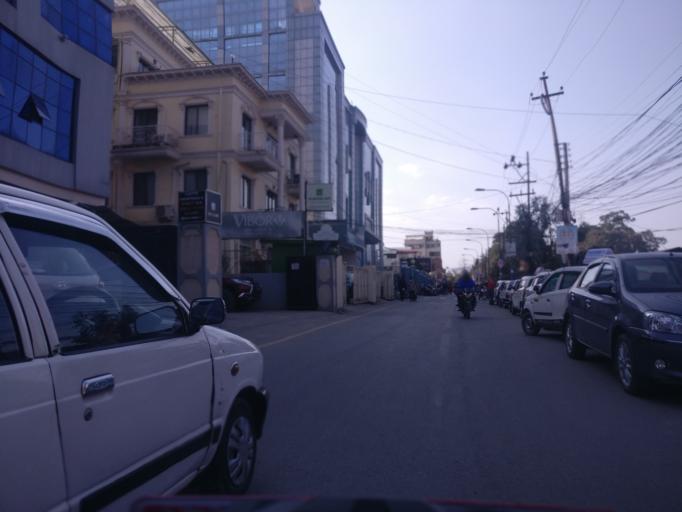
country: NP
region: Central Region
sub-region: Bagmati Zone
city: Patan
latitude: 27.6795
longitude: 85.3203
